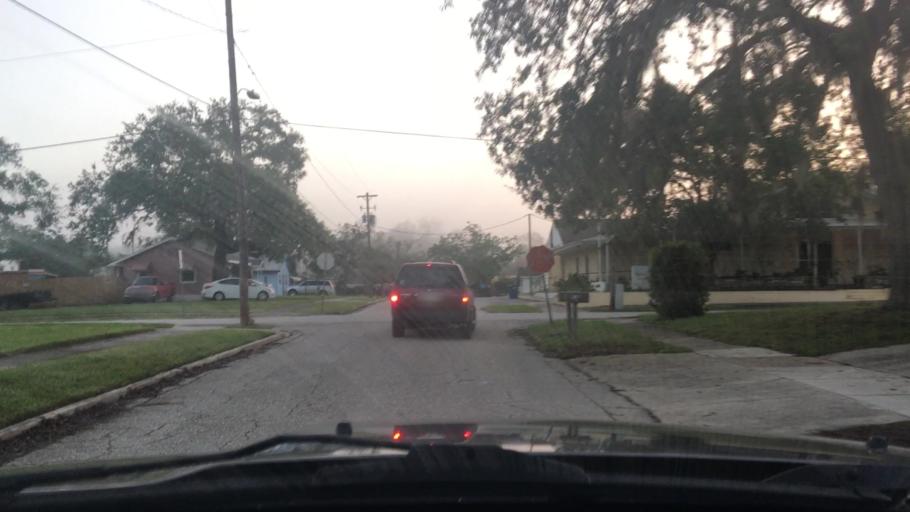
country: US
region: Florida
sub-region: Highlands County
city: Sebring
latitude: 27.4960
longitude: -81.4364
